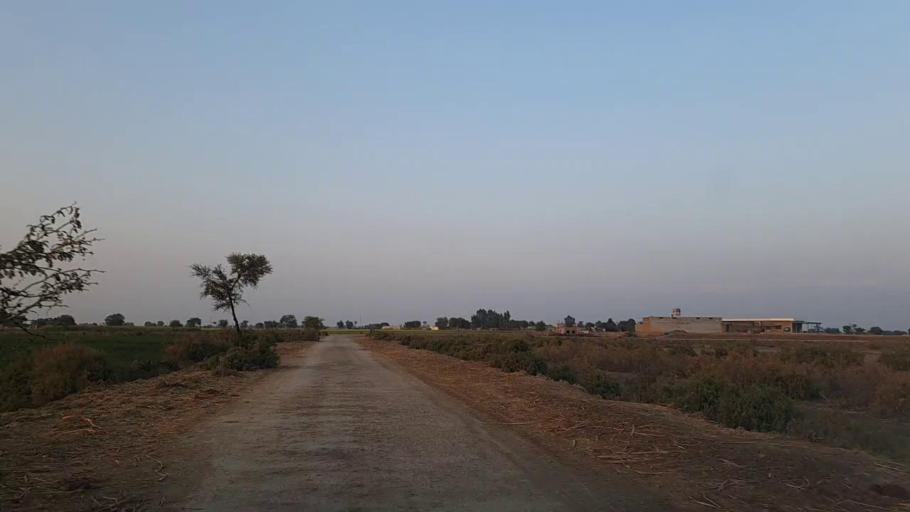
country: PK
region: Sindh
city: Jam Sahib
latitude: 26.3103
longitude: 68.5836
